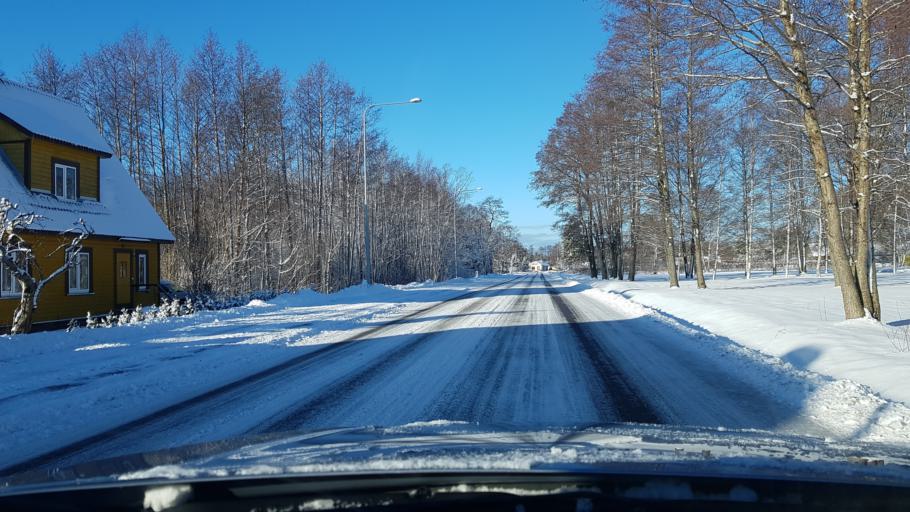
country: EE
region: Hiiumaa
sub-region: Kaerdla linn
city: Kardla
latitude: 58.9878
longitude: 22.7522
